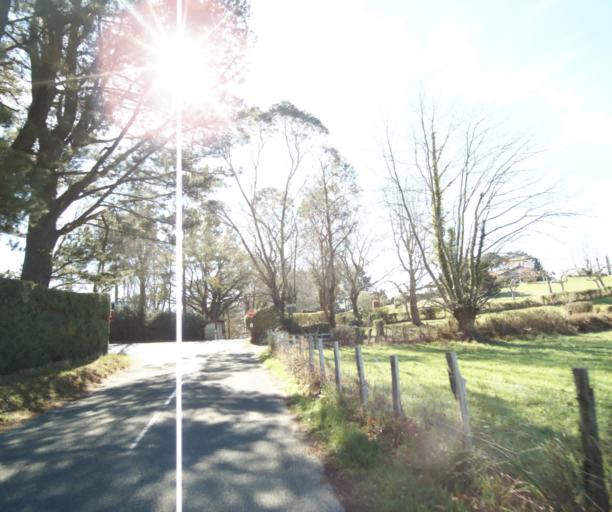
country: FR
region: Aquitaine
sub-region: Departement des Pyrenees-Atlantiques
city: Ciboure
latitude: 43.3531
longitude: -1.6674
